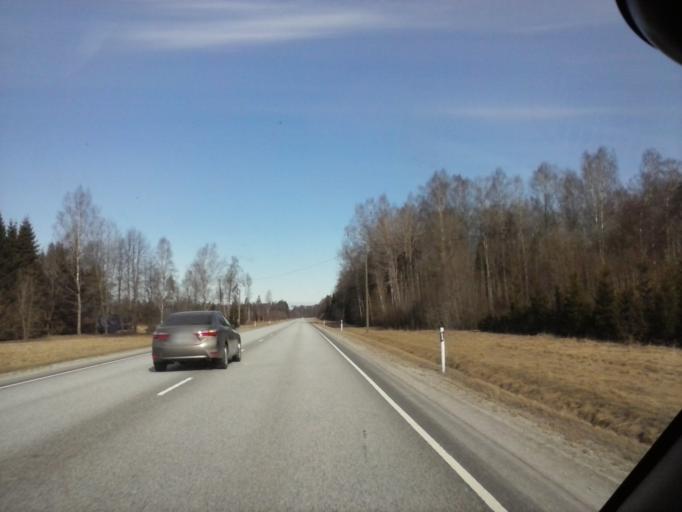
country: EE
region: Jaervamaa
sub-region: Paide linn
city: Paide
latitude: 59.0422
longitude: 25.4430
